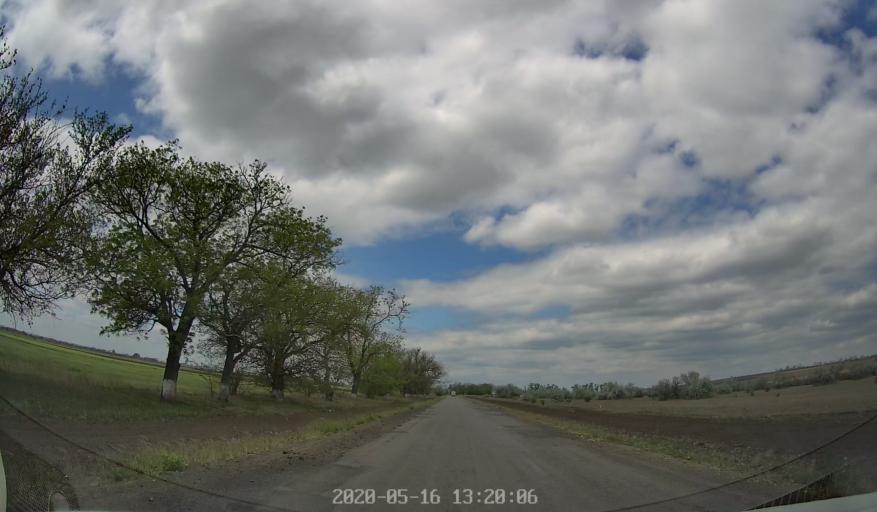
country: UA
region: Odessa
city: Lymanske
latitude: 46.5378
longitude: 30.0525
